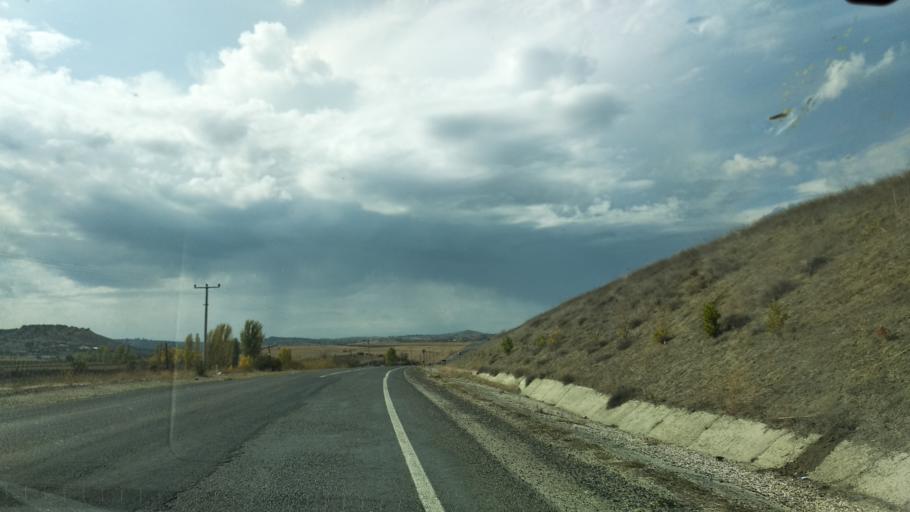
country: TR
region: Bolu
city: Seben
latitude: 40.3985
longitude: 31.5589
